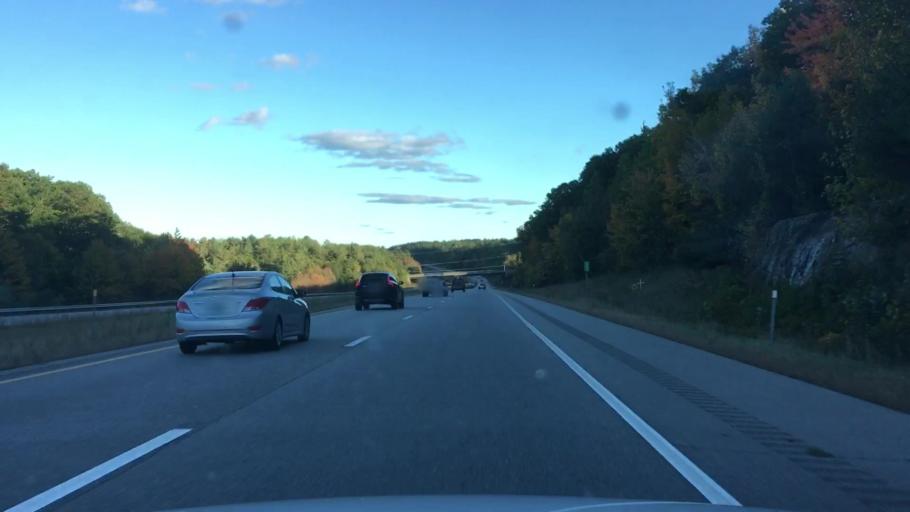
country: US
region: New Hampshire
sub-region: Rockingham County
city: Candia
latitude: 43.0380
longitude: -71.2612
